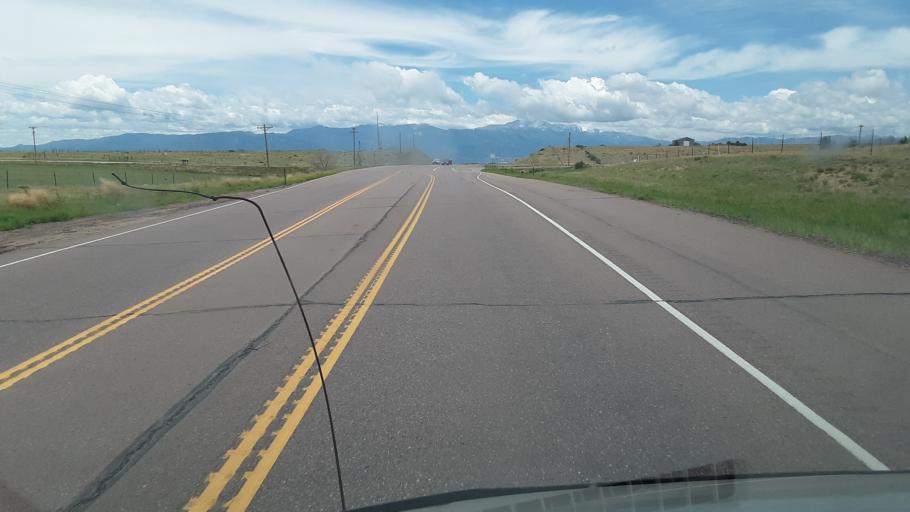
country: US
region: Colorado
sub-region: El Paso County
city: Cimarron Hills
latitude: 38.8387
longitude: -104.5698
